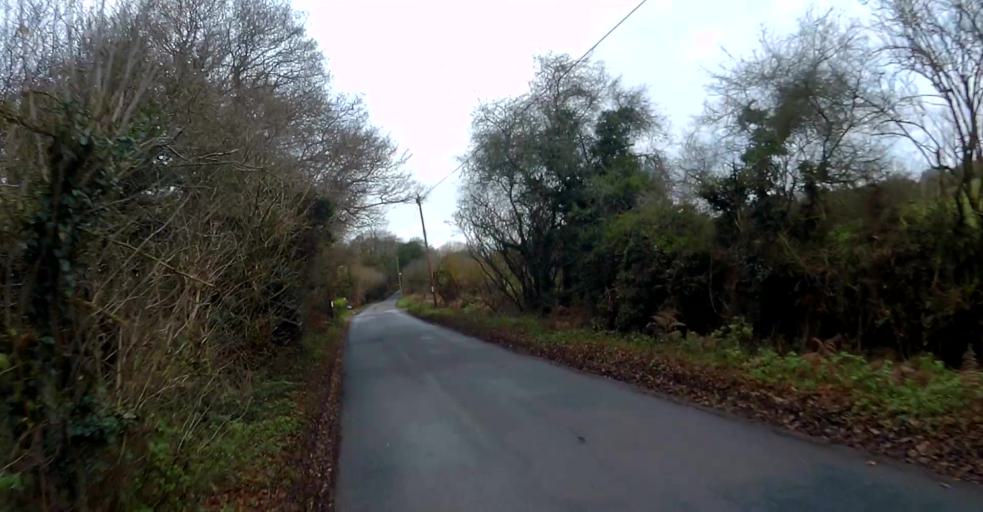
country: GB
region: England
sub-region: Hampshire
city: Basingstoke
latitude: 51.1906
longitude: -1.1570
